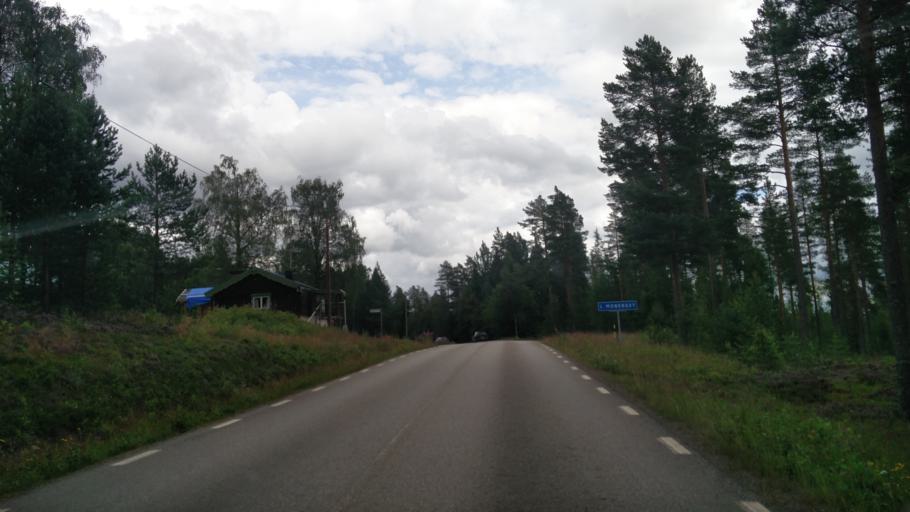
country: NO
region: Hedmark
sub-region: Trysil
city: Innbygda
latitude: 61.1760
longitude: 12.8654
